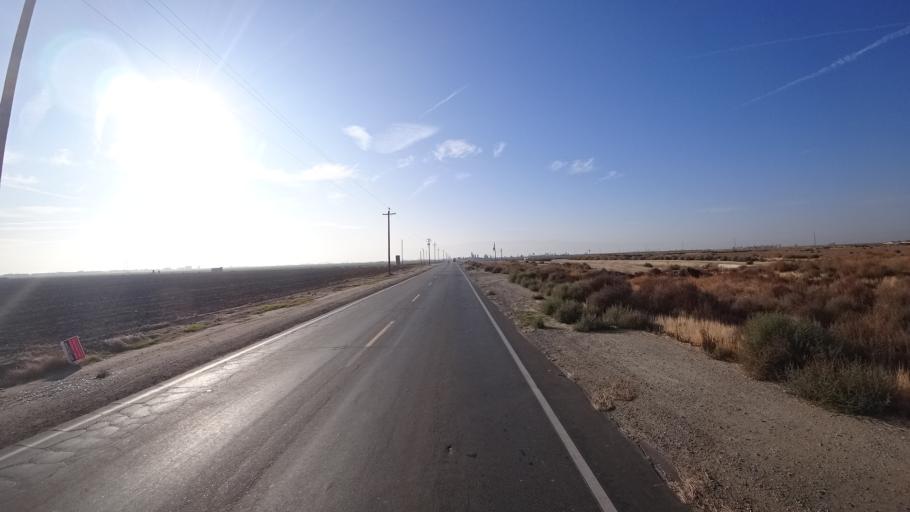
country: US
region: California
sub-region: Kern County
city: Greenfield
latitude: 35.2909
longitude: -119.0922
